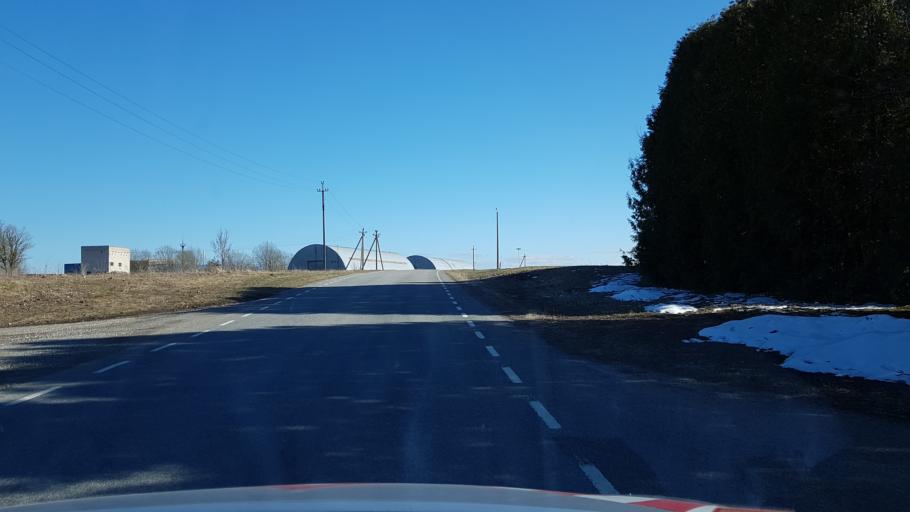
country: EE
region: Laeaene-Virumaa
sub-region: Kadrina vald
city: Kadrina
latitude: 59.3735
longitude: 26.0438
